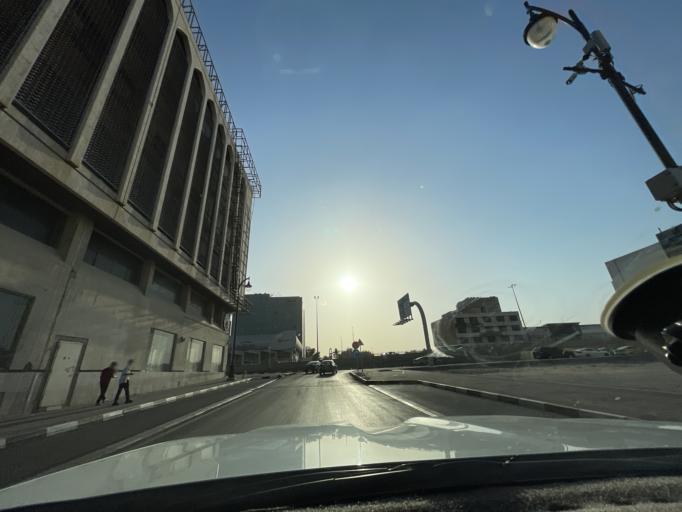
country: SA
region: Eastern Province
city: Khobar
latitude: 26.2881
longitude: 50.2074
